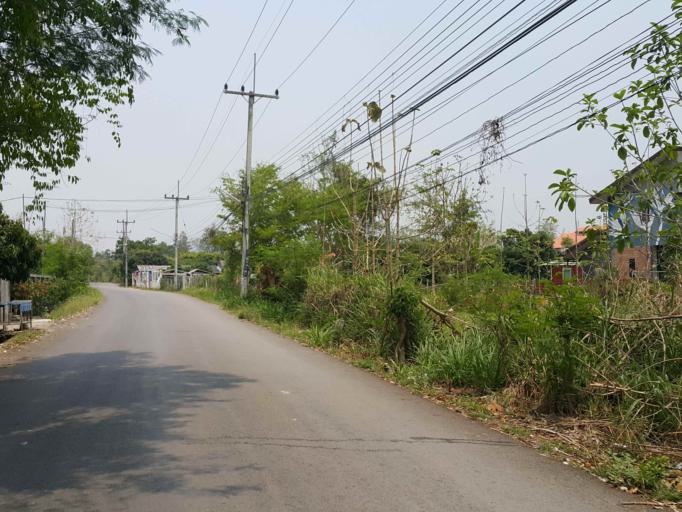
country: TH
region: Chiang Mai
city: San Sai
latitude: 18.9027
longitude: 99.0360
